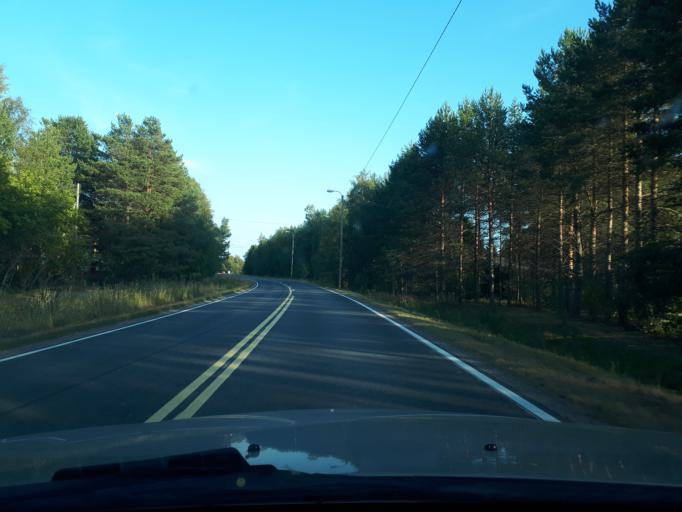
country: FI
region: Northern Ostrobothnia
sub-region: Oulu
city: Oulunsalo
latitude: 64.9876
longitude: 25.2593
